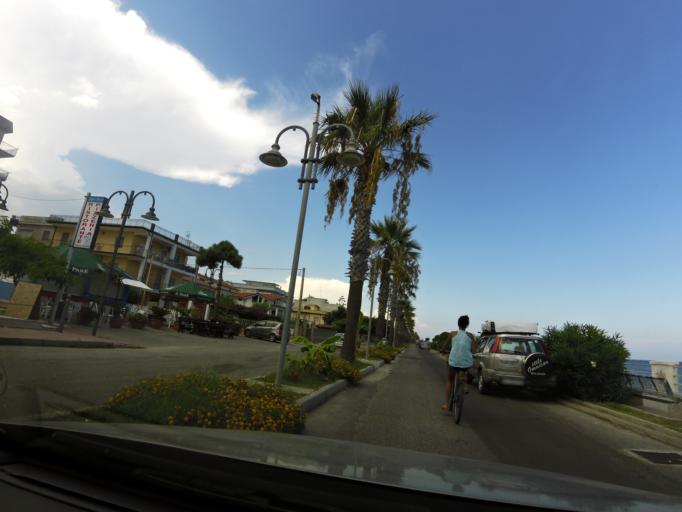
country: IT
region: Calabria
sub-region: Provincia di Reggio Calabria
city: Monasterace Marina
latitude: 38.4373
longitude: 16.5759
